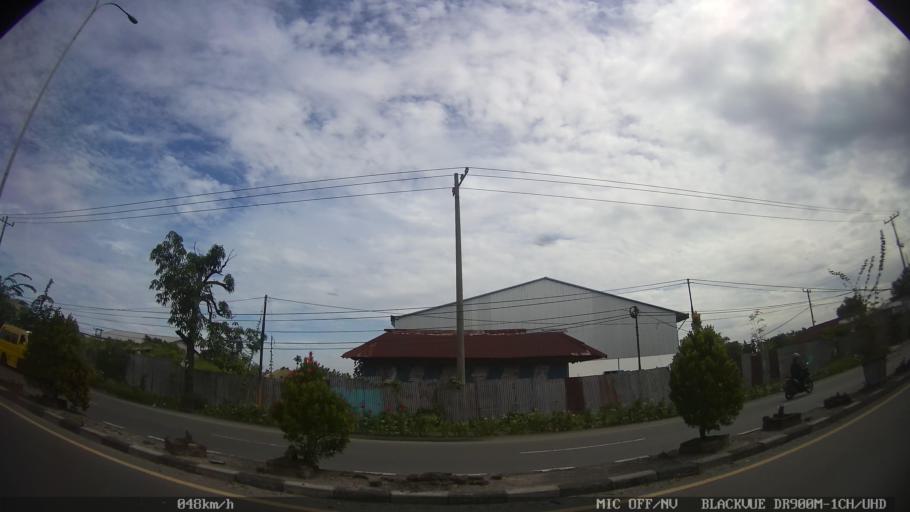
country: ID
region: North Sumatra
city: Sunggal
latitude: 3.5995
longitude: 98.5857
